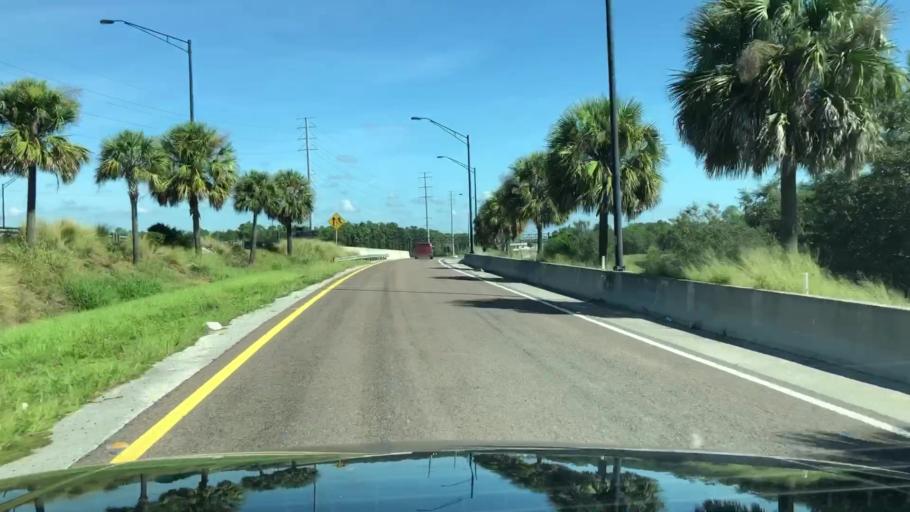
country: US
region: Florida
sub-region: Polk County
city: Citrus Ridge
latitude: 28.3492
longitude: -81.6152
